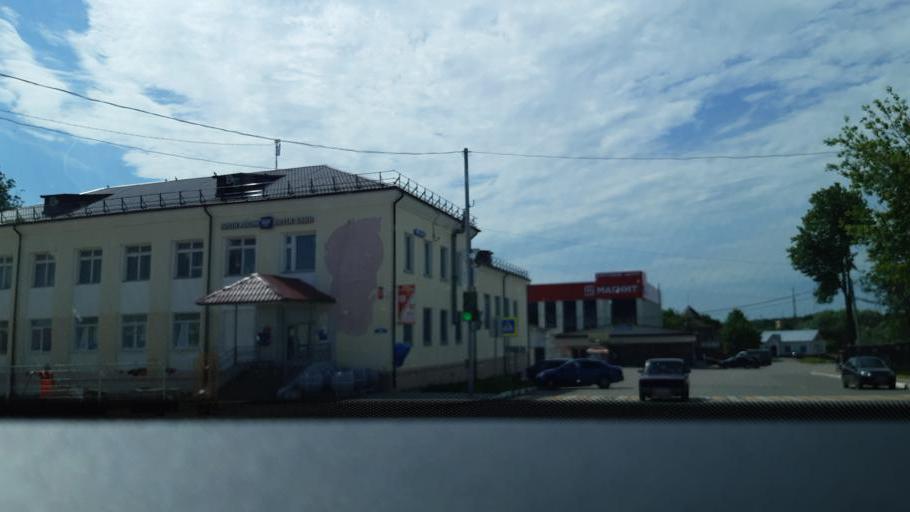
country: RU
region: Kaluga
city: Medyn'
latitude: 54.9678
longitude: 35.8571
